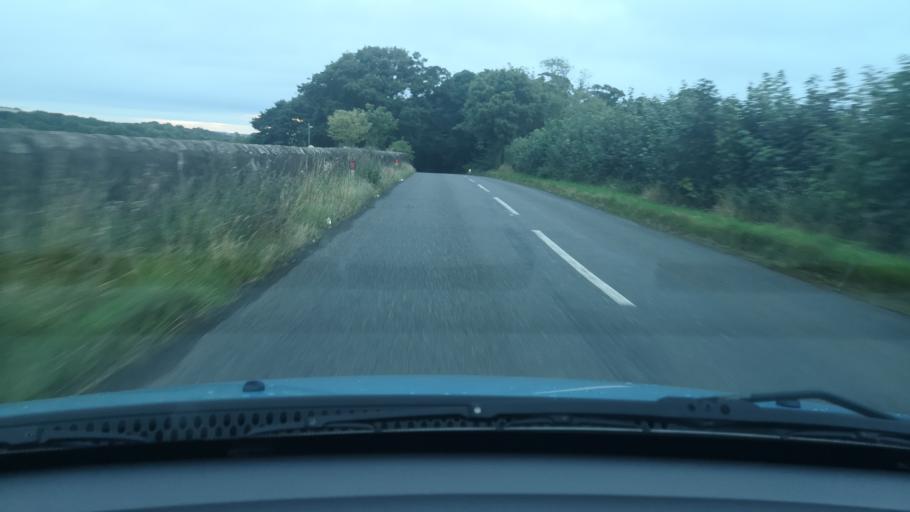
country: GB
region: England
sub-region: Doncaster
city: Campsall
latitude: 53.6161
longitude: -1.1890
